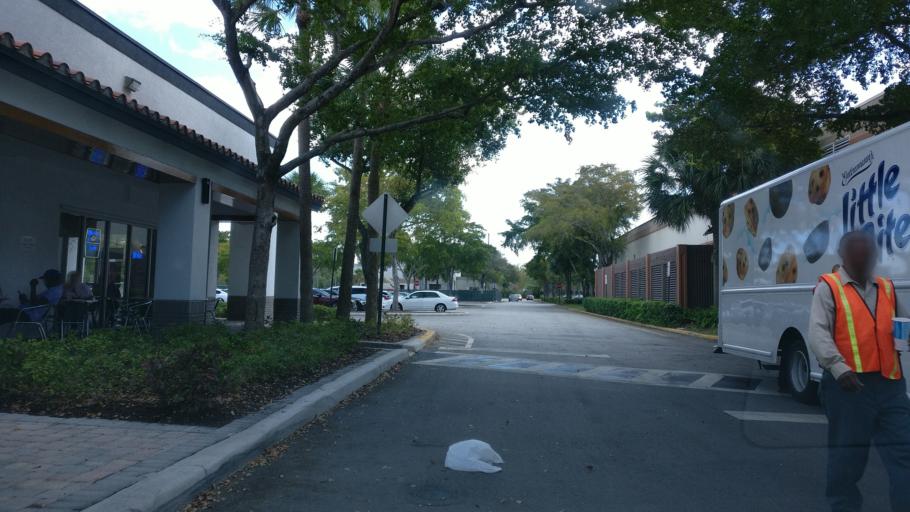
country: US
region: Florida
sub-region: Broward County
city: Pine Island Ridge
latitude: 26.1070
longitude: -80.2522
